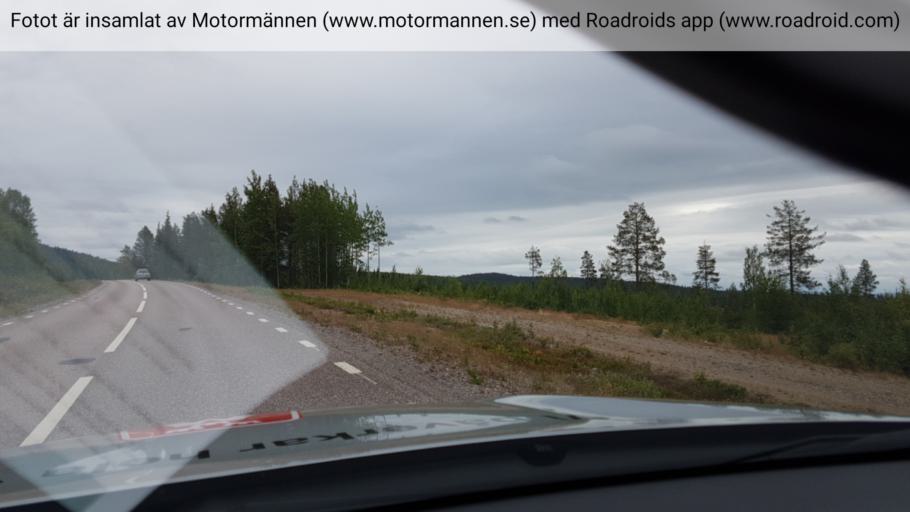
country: SE
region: Norrbotten
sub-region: Gallivare Kommun
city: Gaellivare
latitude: 67.0458
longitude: 21.6217
